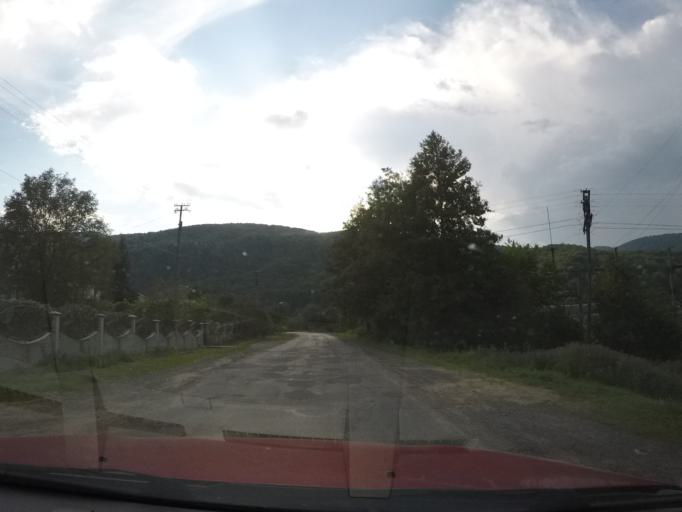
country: UA
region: Zakarpattia
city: Velykyi Bereznyi
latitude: 48.9842
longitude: 22.6323
